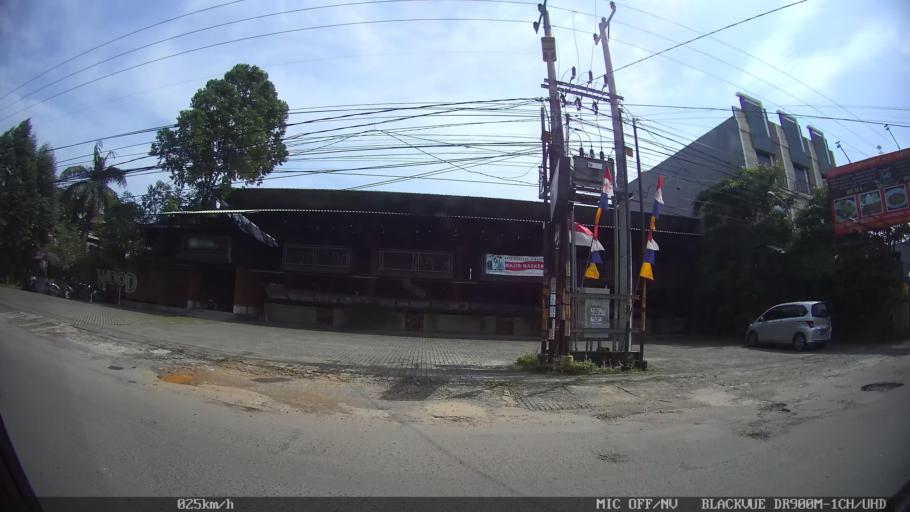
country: ID
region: Lampung
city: Kedaton
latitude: -5.3912
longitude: 105.2802
